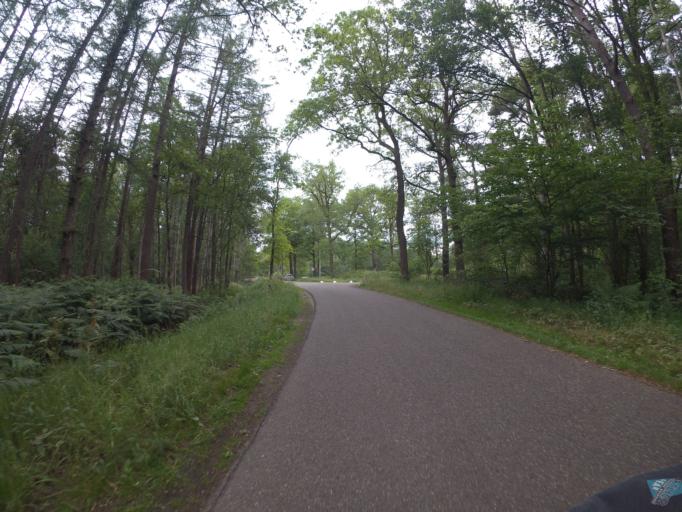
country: NL
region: North Brabant
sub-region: Gemeente Best
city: Best
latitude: 51.5321
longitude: 5.3518
